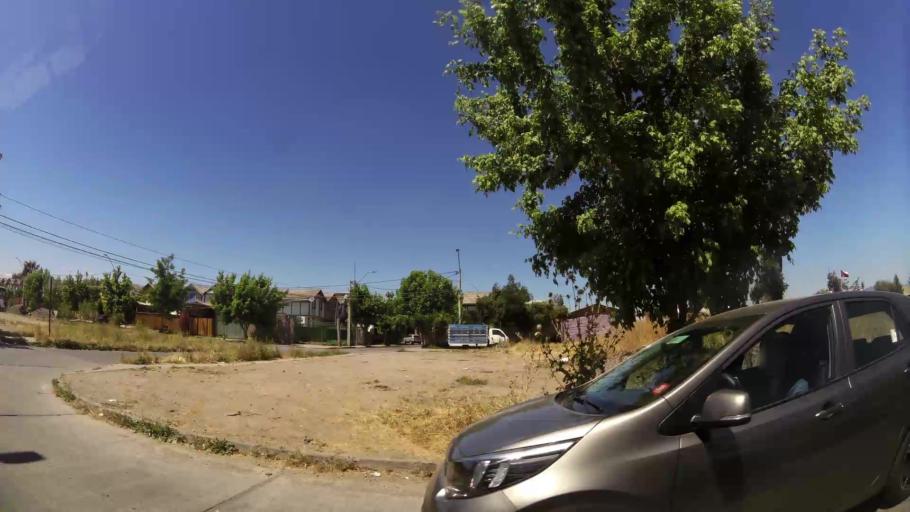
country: CL
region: Santiago Metropolitan
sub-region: Provincia de Maipo
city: San Bernardo
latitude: -33.6254
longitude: -70.7075
